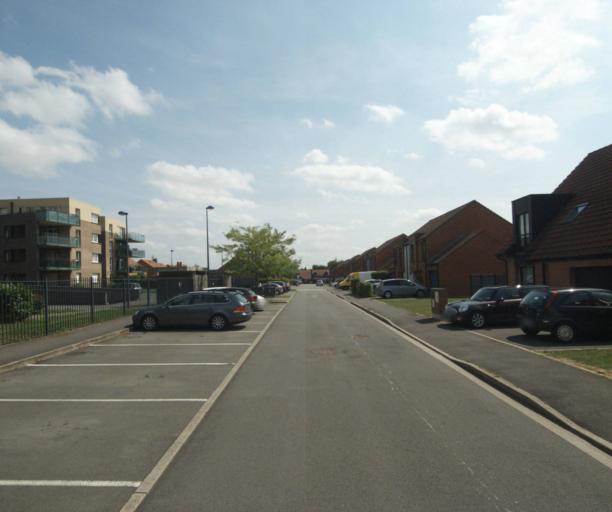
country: FR
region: Nord-Pas-de-Calais
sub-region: Departement du Nord
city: Hem
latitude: 50.6513
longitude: 3.1918
